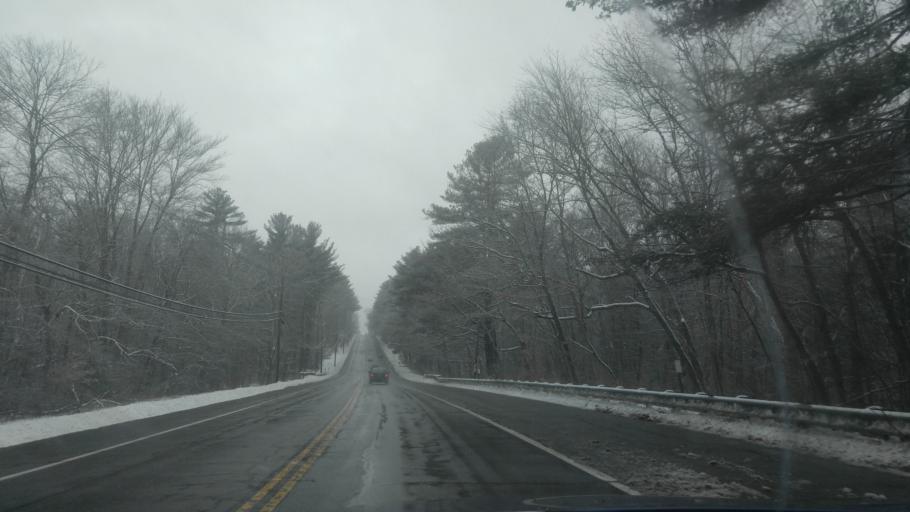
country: US
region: Rhode Island
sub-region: Providence County
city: Foster
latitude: 41.8214
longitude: -71.7045
